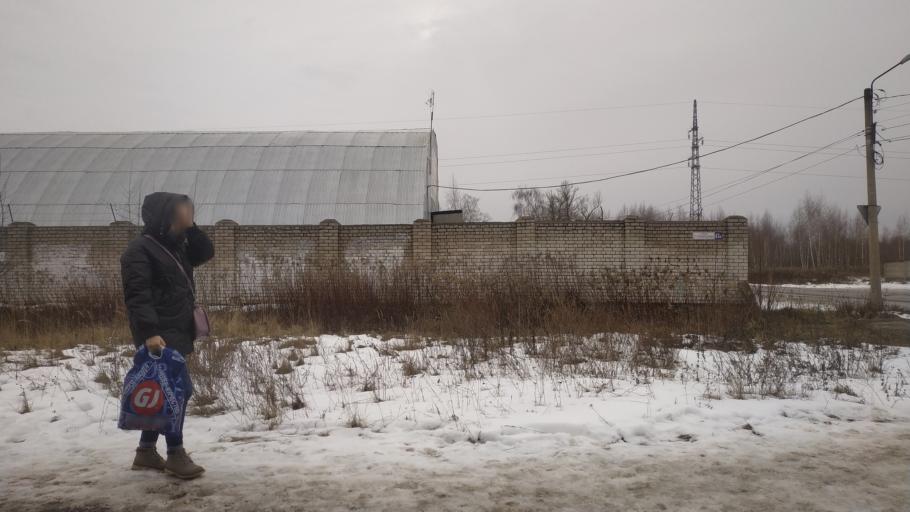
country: RU
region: Tverskaya
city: Tver
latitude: 56.8839
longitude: 35.8856
